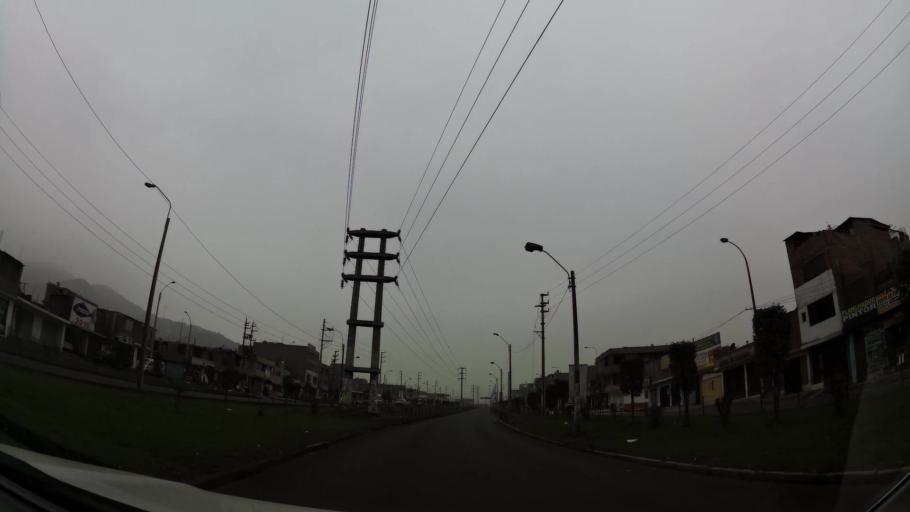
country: PE
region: Lima
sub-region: Lima
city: Urb. Santo Domingo
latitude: -11.9395
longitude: -76.9788
